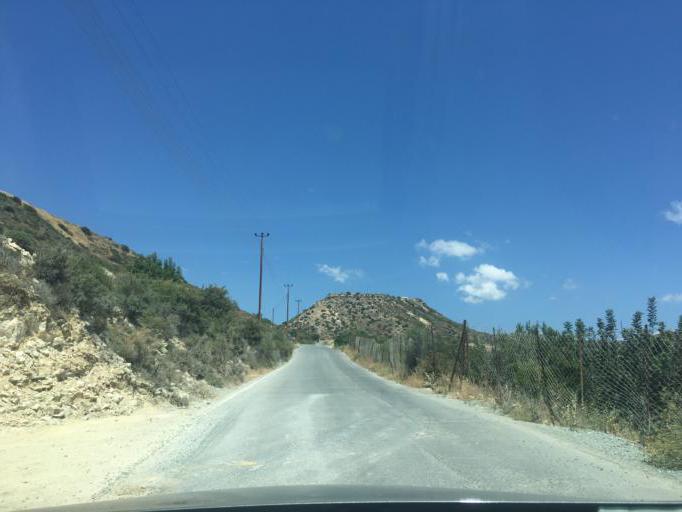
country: CY
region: Limassol
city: Mouttagiaka
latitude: 34.7220
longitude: 33.0773
